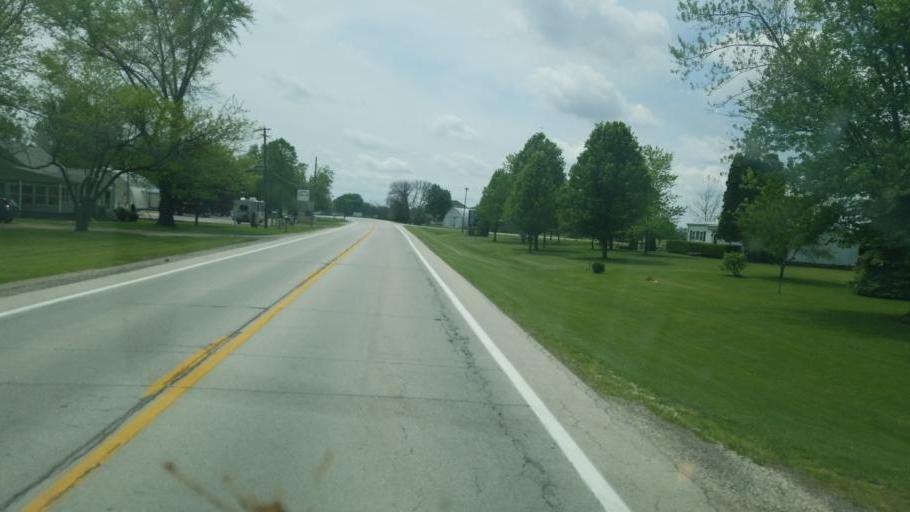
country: US
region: Ohio
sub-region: Sandusky County
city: Fremont
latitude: 41.4133
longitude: -83.0958
